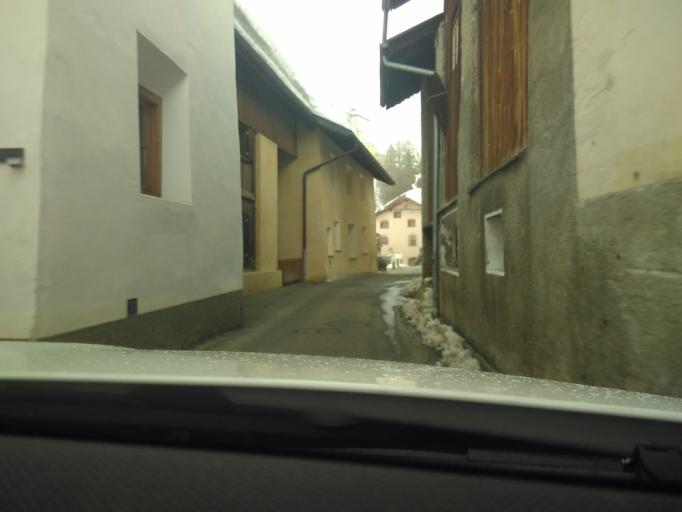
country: CH
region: Grisons
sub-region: Inn District
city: Scuol
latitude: 46.7796
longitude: 10.2654
